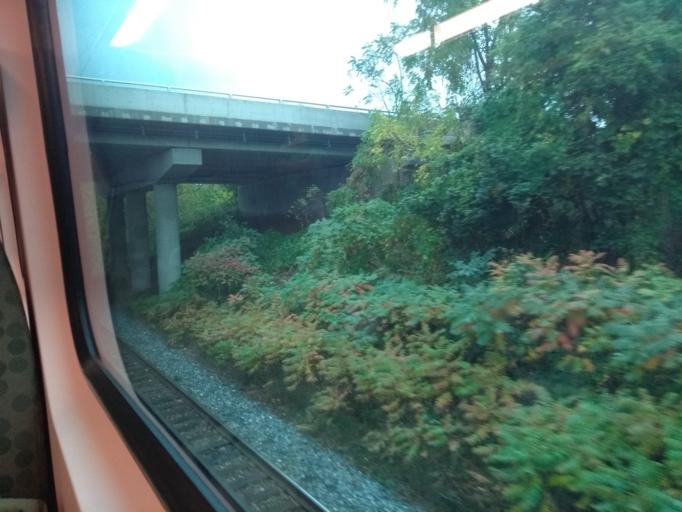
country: CA
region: Ontario
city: Oakville
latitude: 43.1954
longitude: -79.5549
